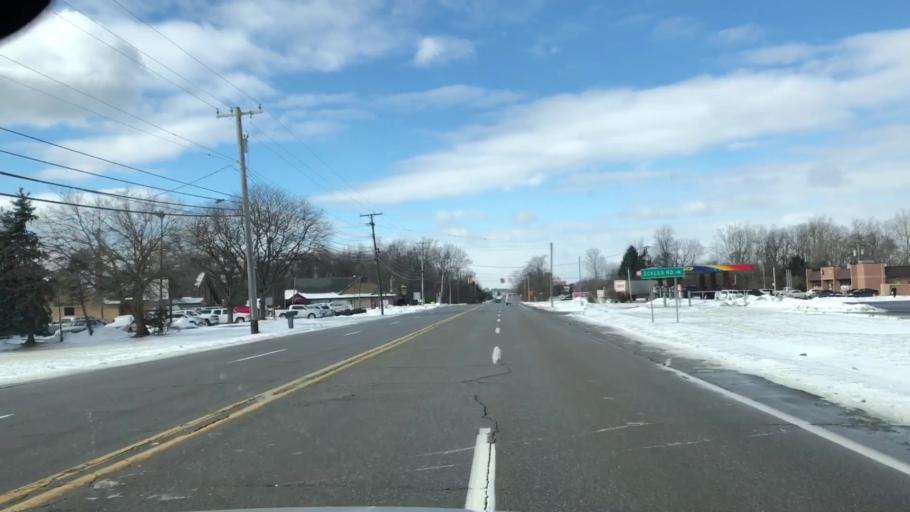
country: US
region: Michigan
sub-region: Wayne County
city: Plymouth
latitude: 42.3715
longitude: -83.4286
